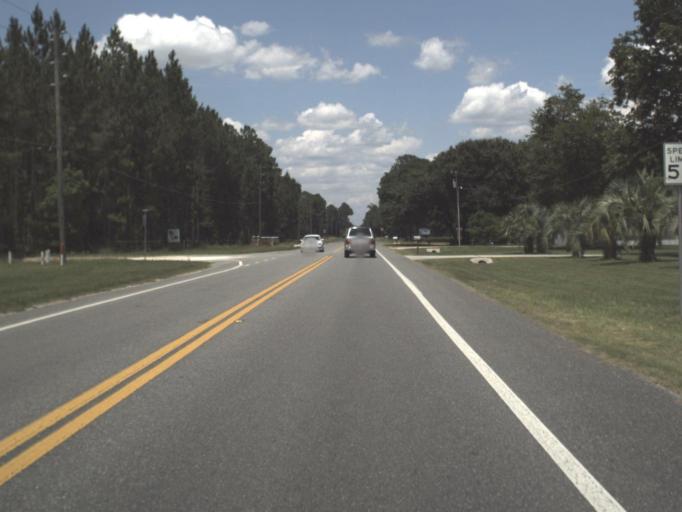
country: US
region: Florida
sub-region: Columbia County
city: Lake City
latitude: 30.1201
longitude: -82.7265
